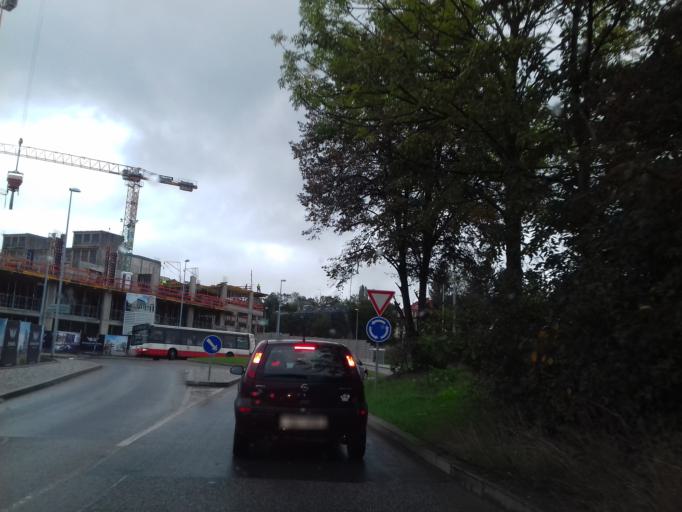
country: CZ
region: Praha
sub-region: Praha 1
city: Mala Strana
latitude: 50.0573
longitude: 14.3706
